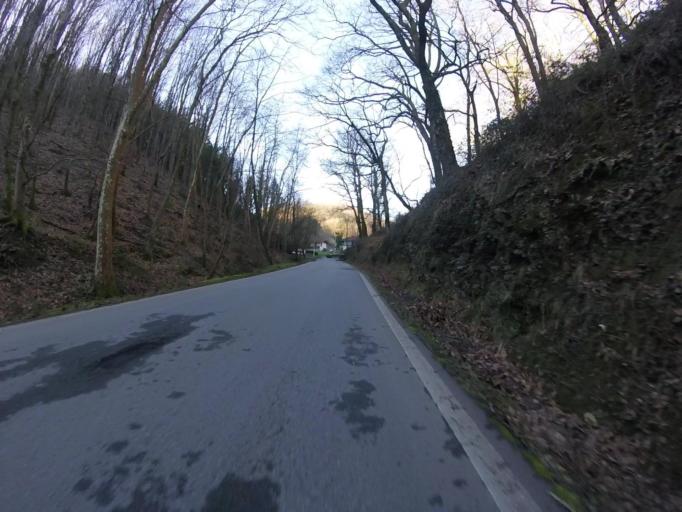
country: ES
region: Navarre
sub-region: Provincia de Navarra
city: Lesaka
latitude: 43.2531
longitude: -1.7228
